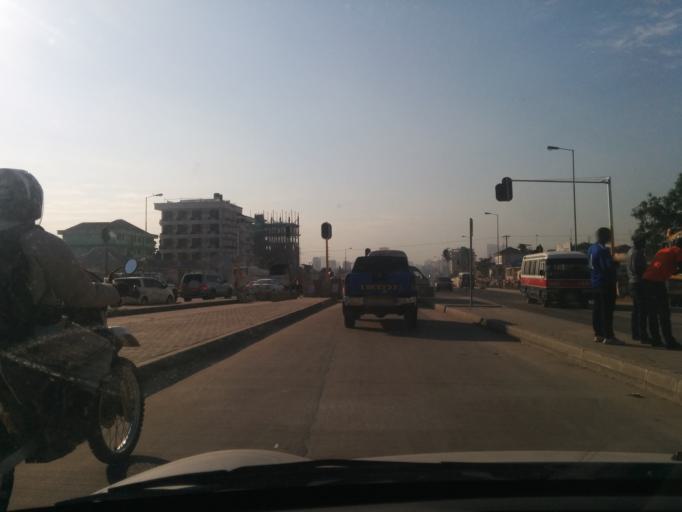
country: TZ
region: Dar es Salaam
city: Magomeni
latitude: -6.8085
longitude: 39.2607
